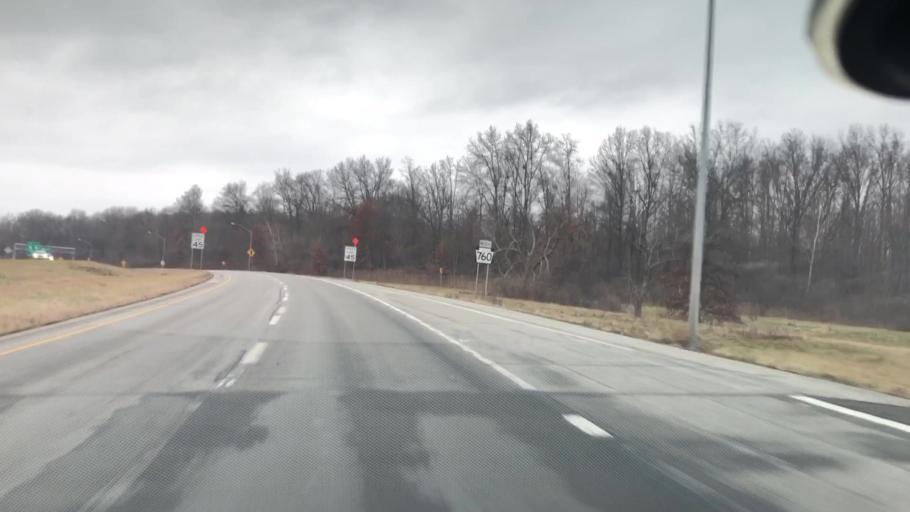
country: US
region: Pennsylvania
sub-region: Mercer County
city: Hermitage
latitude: 41.1859
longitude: -80.4448
